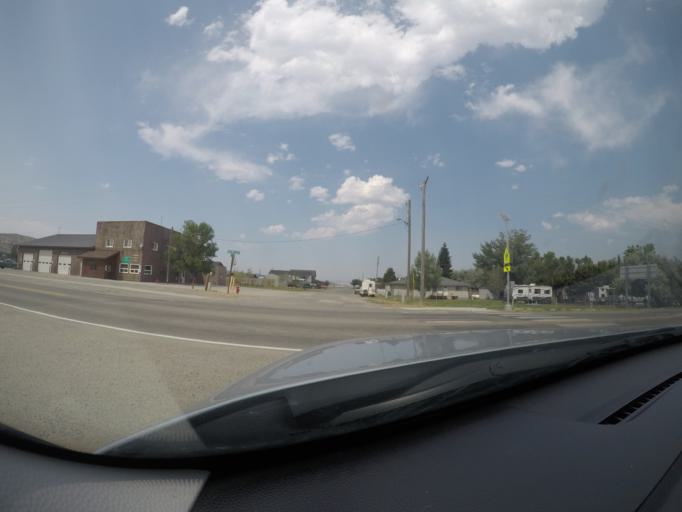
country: US
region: Montana
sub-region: Madison County
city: Virginia City
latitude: 45.3490
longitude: -111.7345
